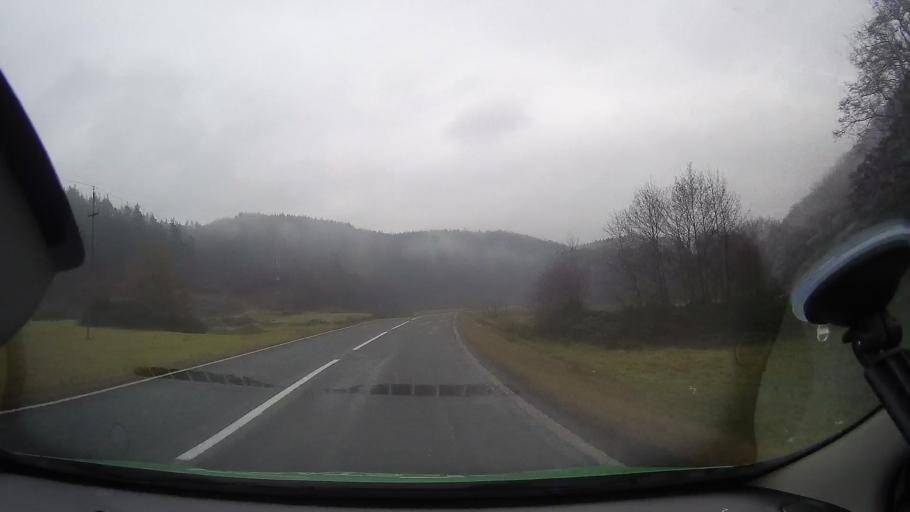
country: RO
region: Arad
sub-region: Comuna Plescuta
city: Plescuta
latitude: 46.3164
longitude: 22.4574
